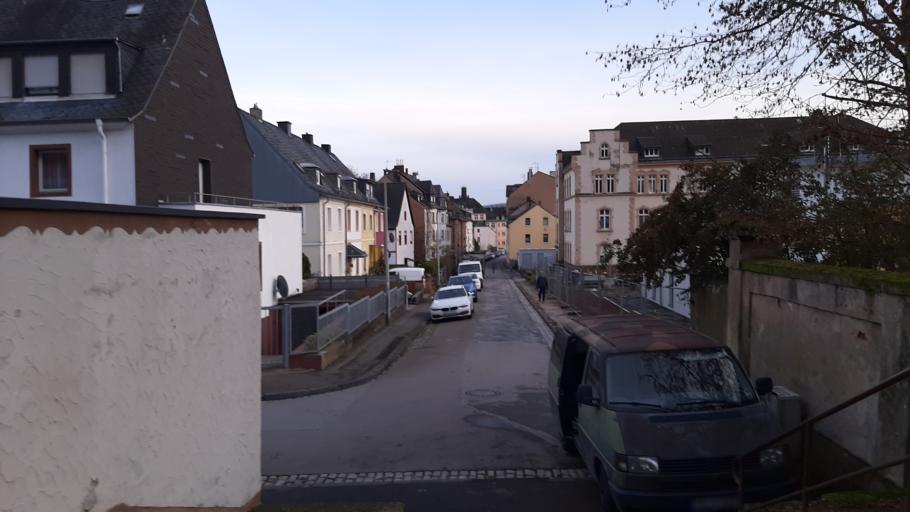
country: DE
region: Rheinland-Pfalz
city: Trier
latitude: 49.7540
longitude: 6.6173
